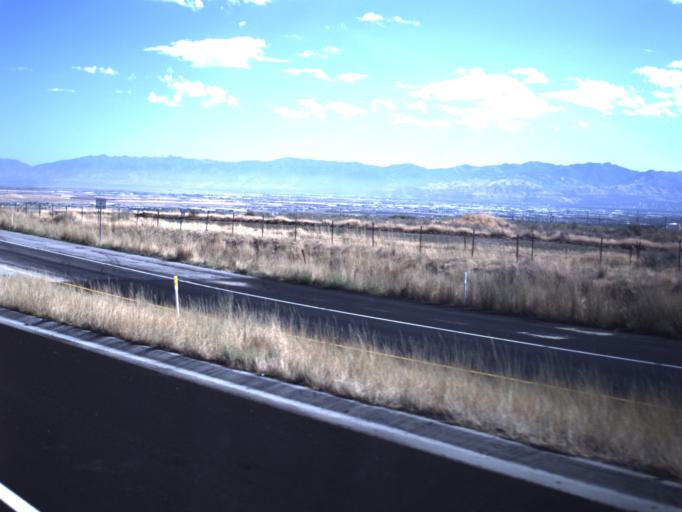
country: US
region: Utah
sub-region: Salt Lake County
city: Magna
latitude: 40.6695
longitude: -112.0919
